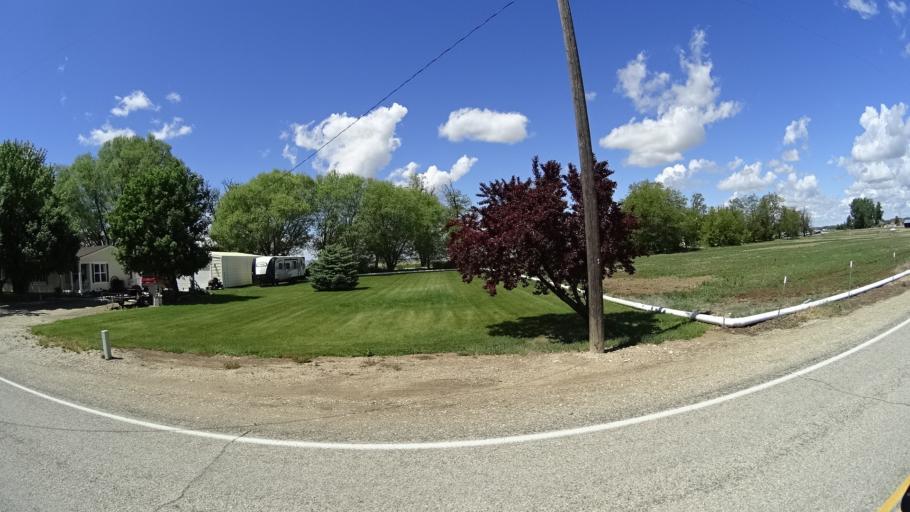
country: US
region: Idaho
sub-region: Ada County
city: Kuna
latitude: 43.4997
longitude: -116.3543
